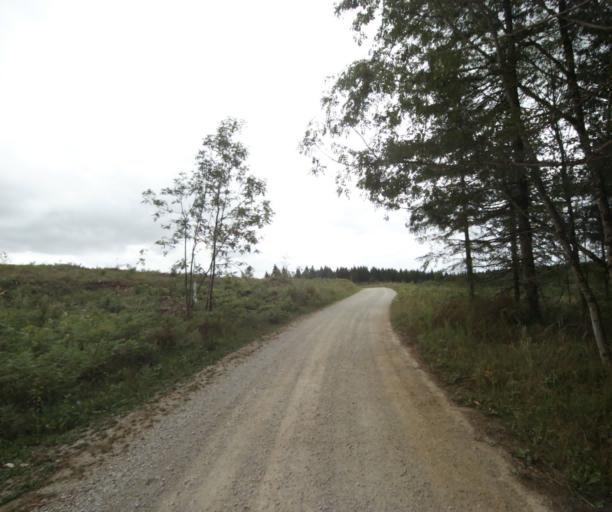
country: FR
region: Midi-Pyrenees
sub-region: Departement du Tarn
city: Soreze
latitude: 43.4277
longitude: 2.1205
